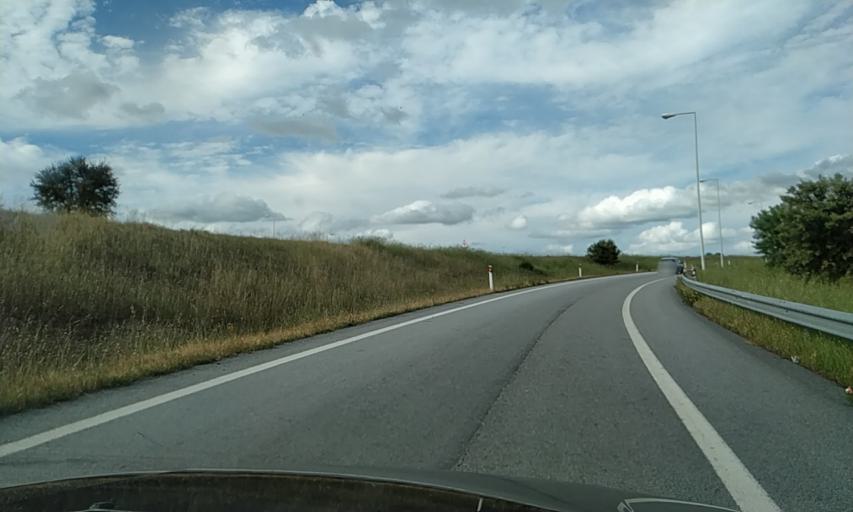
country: PT
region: Evora
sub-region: Evora
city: Evora
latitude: 38.6464
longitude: -7.8562
